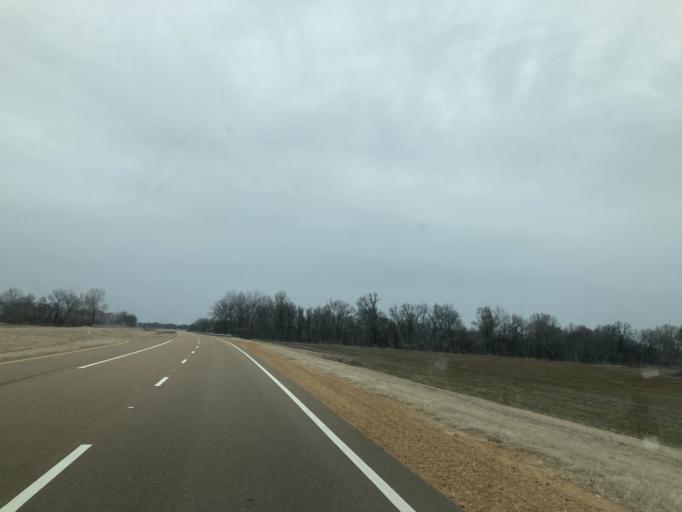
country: US
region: Mississippi
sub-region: Humphreys County
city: Belzoni
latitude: 33.0744
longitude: -90.4762
